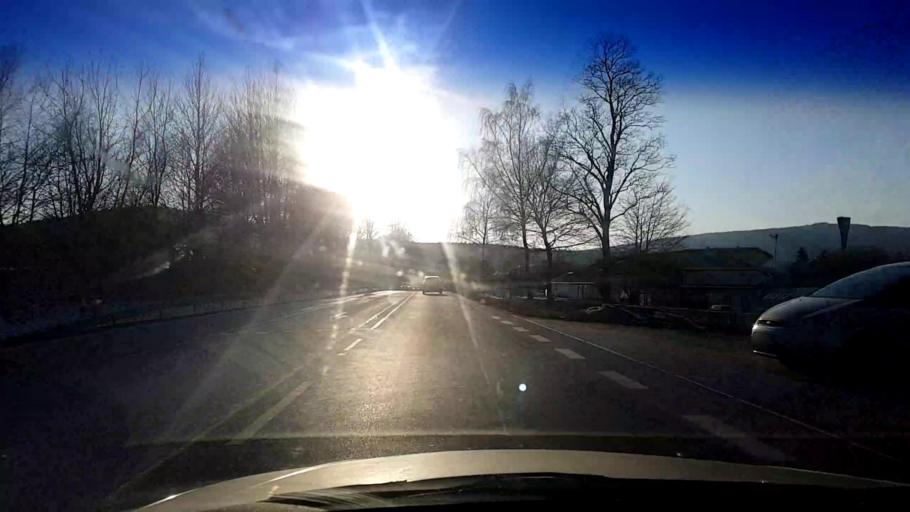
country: DE
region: Bavaria
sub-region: Upper Franconia
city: Trostau
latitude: 50.0156
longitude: 11.9572
